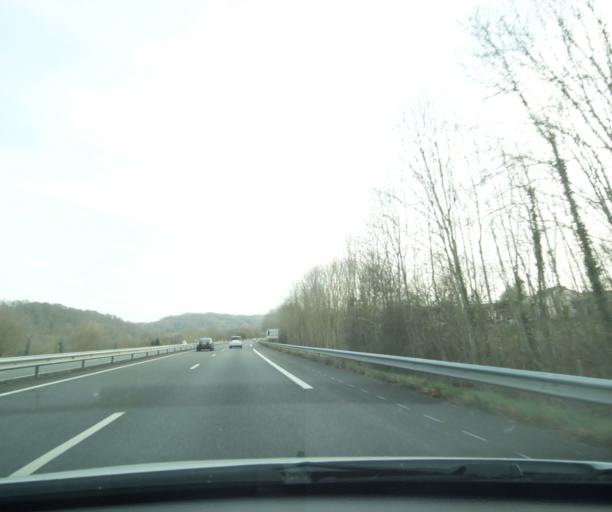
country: FR
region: Midi-Pyrenees
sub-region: Departement des Hautes-Pyrenees
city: Tournay
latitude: 43.1875
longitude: 0.2221
